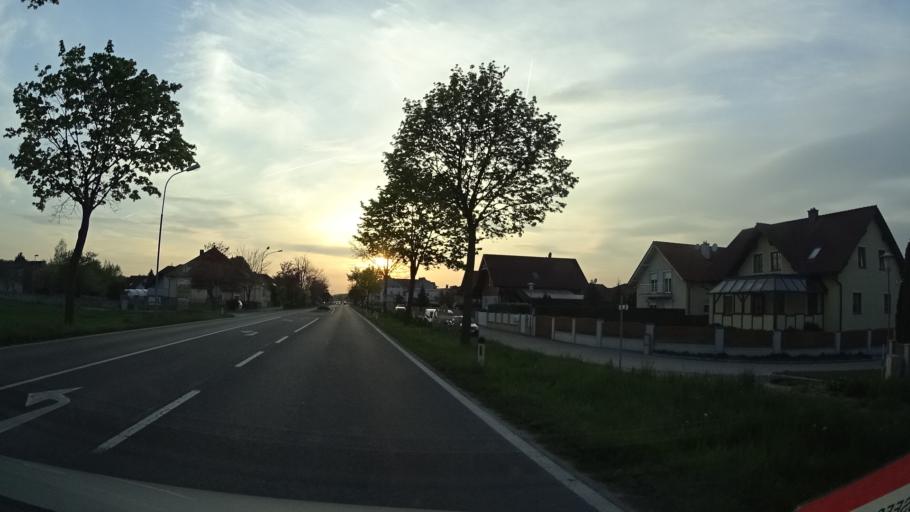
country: AT
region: Lower Austria
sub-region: Politischer Bezirk Korneuburg
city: Spillern
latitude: 48.3760
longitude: 16.2732
